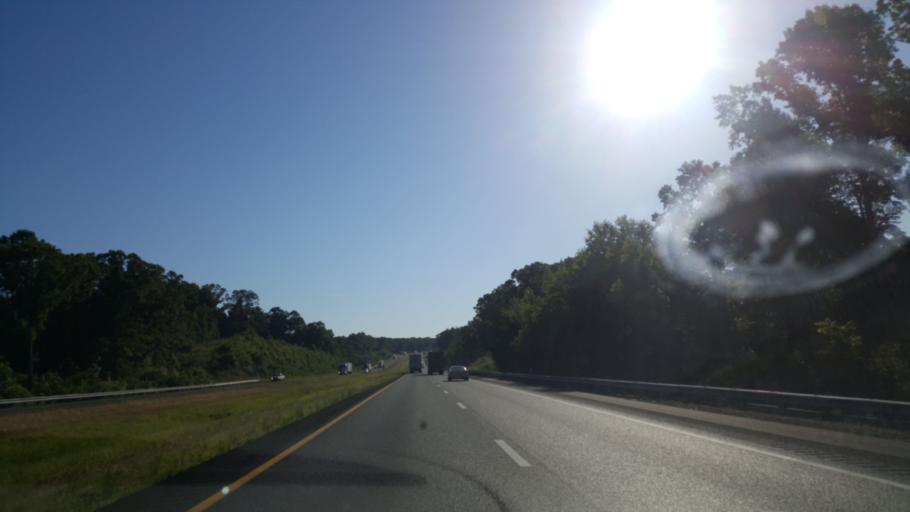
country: US
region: Tennessee
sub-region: Humphreys County
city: New Johnsonville
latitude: 35.8640
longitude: -88.0422
